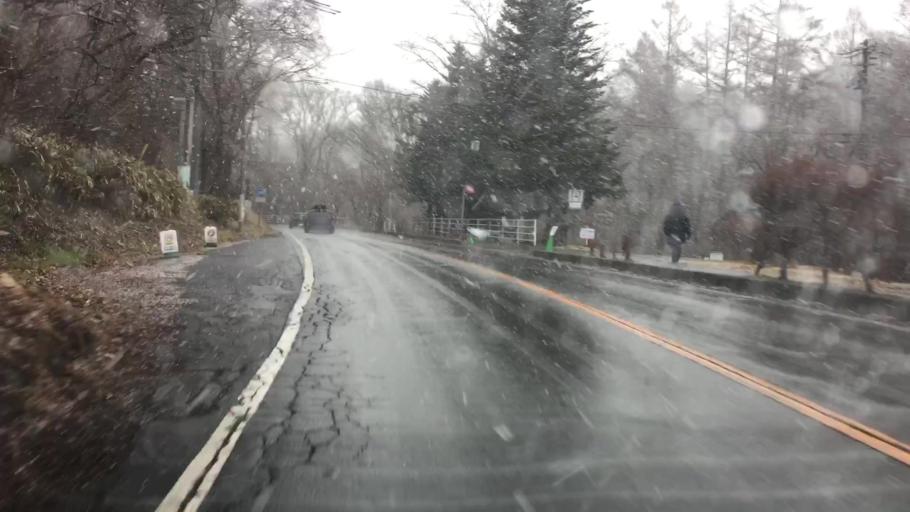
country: JP
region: Nagano
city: Komoro
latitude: 36.3592
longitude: 138.5900
